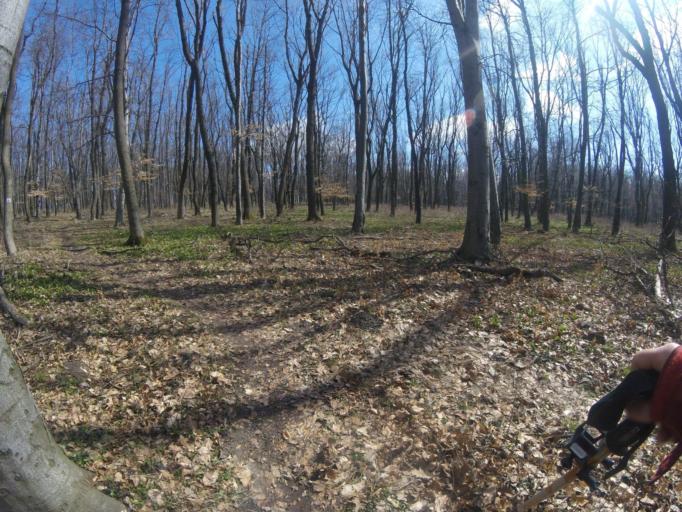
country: HU
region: Komarom-Esztergom
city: Tardos
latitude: 47.6789
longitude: 18.4837
